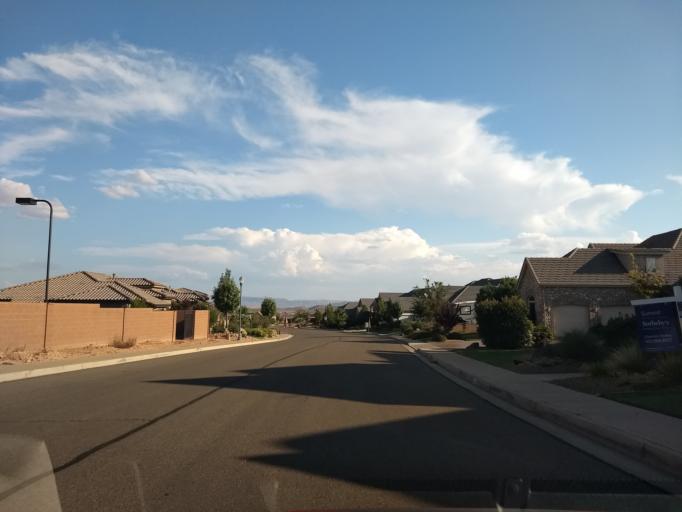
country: US
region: Utah
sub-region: Washington County
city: Saint George
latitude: 37.1055
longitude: -113.5501
